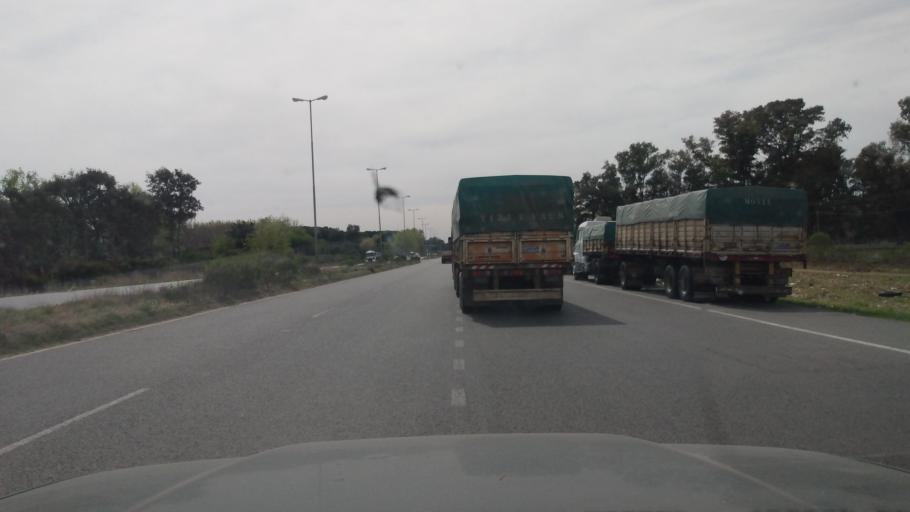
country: AR
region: Buenos Aires
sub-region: Partido de Lujan
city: Lujan
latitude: -34.4680
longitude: -59.0665
